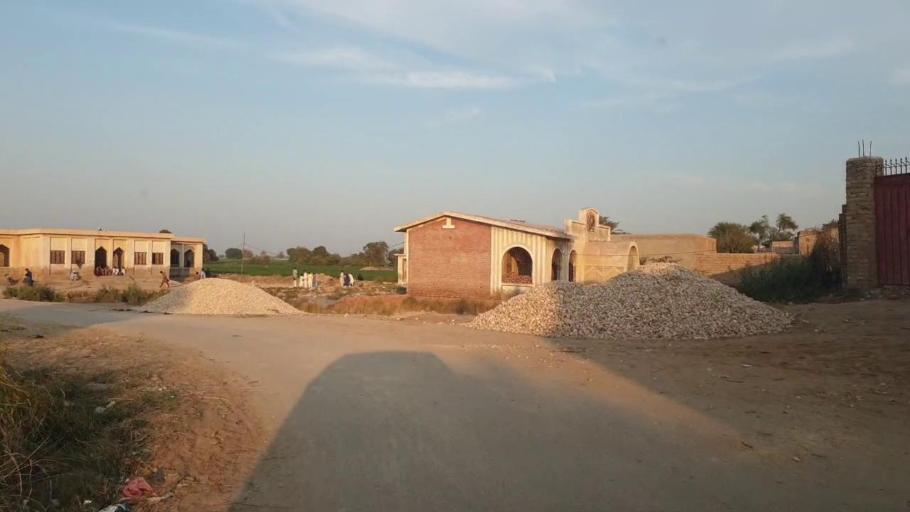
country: PK
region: Sindh
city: Shahpur Chakar
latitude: 26.1742
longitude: 68.6144
